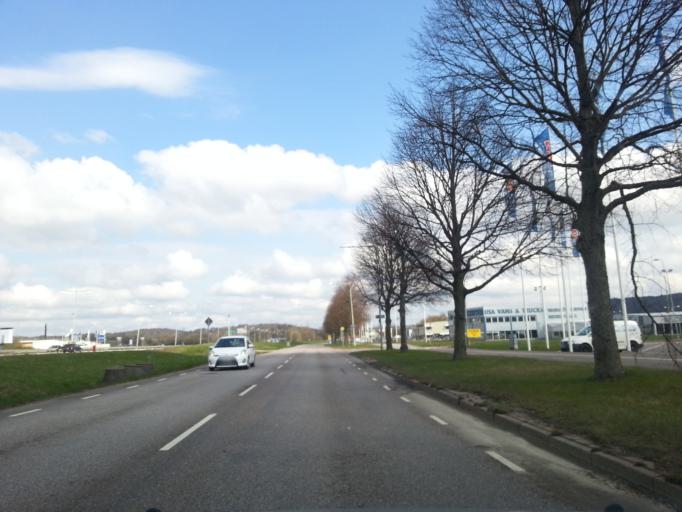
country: SE
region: Vaestra Goetaland
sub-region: Goteborg
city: Hammarkullen
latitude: 57.7812
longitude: 11.9998
